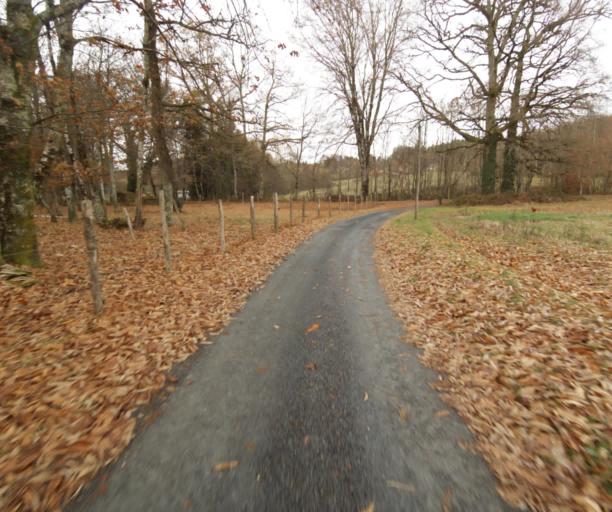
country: FR
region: Limousin
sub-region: Departement de la Correze
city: Chameyrat
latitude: 45.2663
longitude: 1.6964
